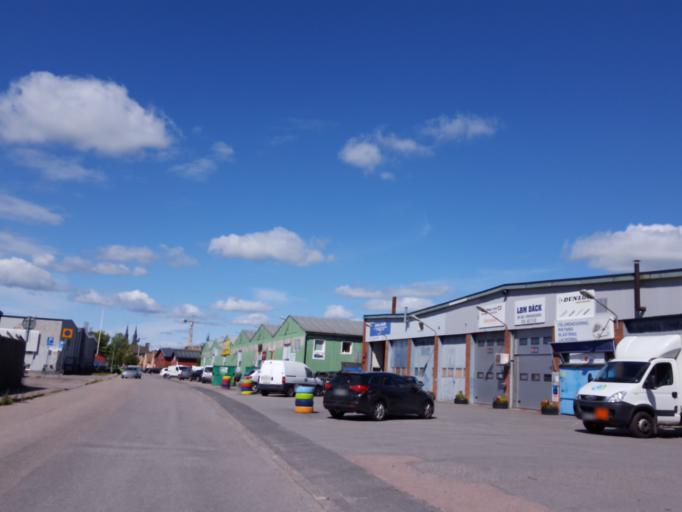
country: SE
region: Uppsala
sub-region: Uppsala Kommun
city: Uppsala
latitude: 59.8539
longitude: 17.6649
